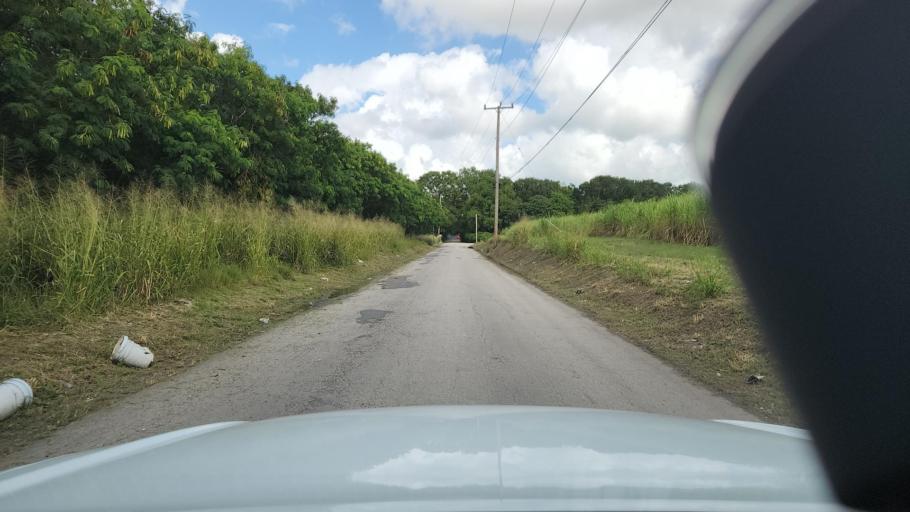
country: BB
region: Saint Michael
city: Bridgetown
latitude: 13.1130
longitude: -59.5888
